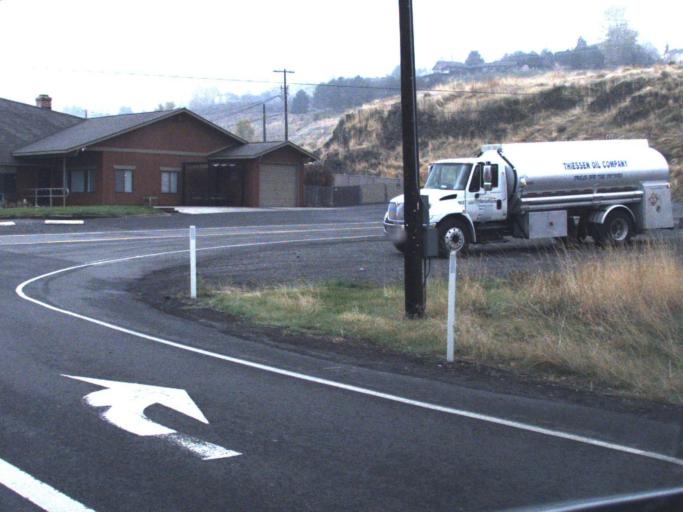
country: US
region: Washington
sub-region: Asotin County
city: Clarkston Heights-Vineland
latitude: 46.3682
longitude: -117.0632
